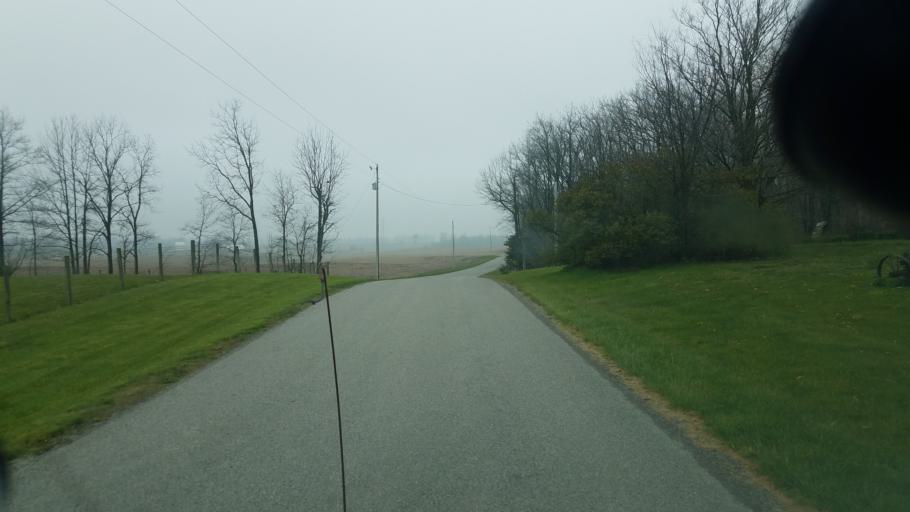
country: US
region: Ohio
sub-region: Logan County
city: Northwood
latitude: 40.5341
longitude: -83.6640
